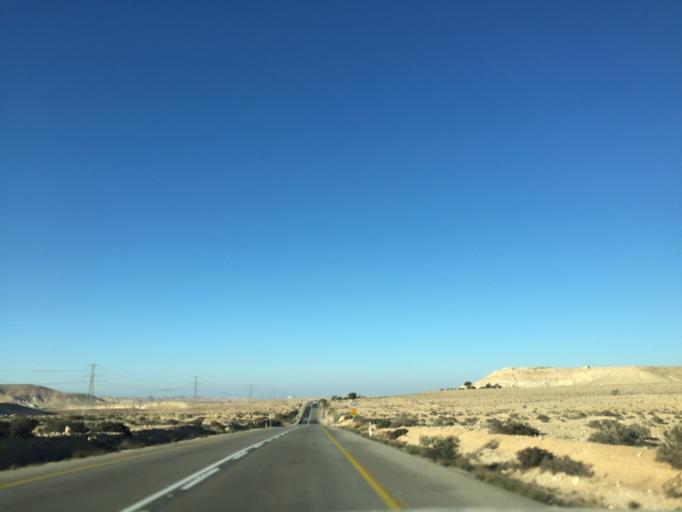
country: IL
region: Southern District
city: Midreshet Ben-Gurion
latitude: 30.7778
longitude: 34.7696
